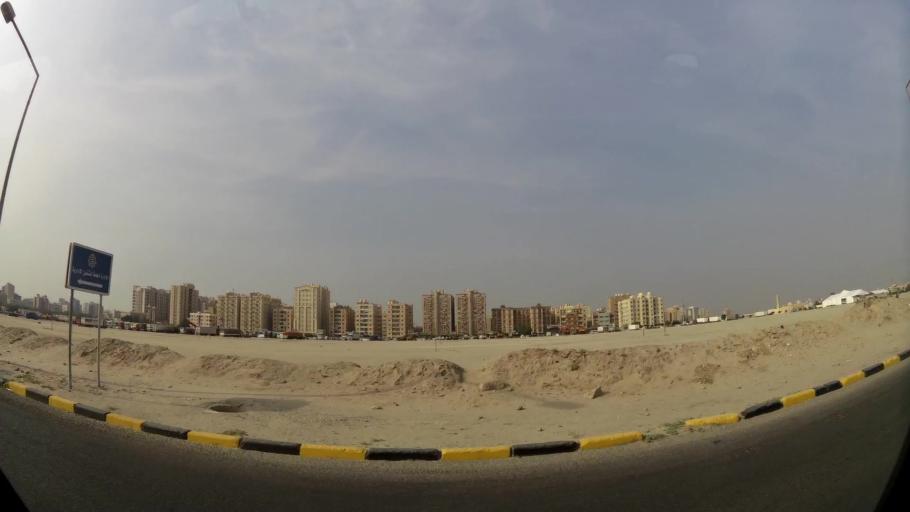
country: KW
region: Al Farwaniyah
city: Janub as Surrah
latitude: 29.2735
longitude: 47.9753
